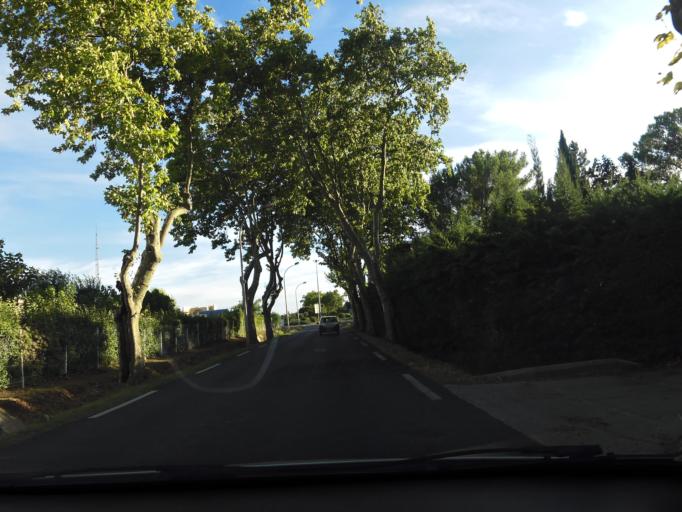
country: FR
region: Languedoc-Roussillon
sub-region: Departement de l'Herault
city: Saint-Mathieu-de-Treviers
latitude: 43.7627
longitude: 3.8642
